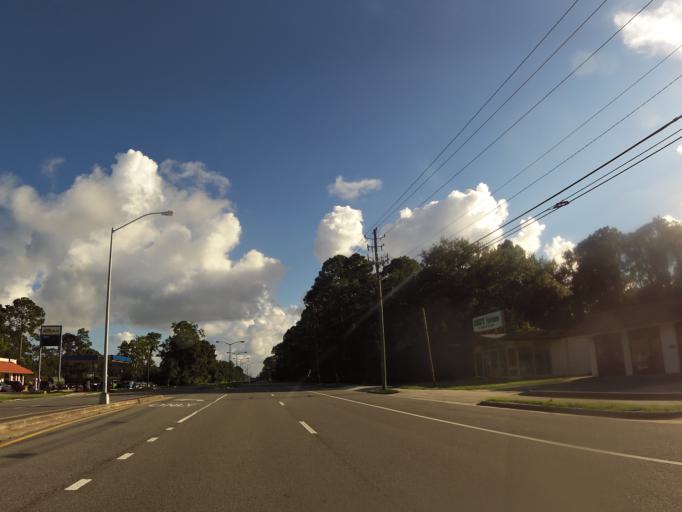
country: US
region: Georgia
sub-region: Glynn County
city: Country Club Estates
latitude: 31.2239
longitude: -81.4779
